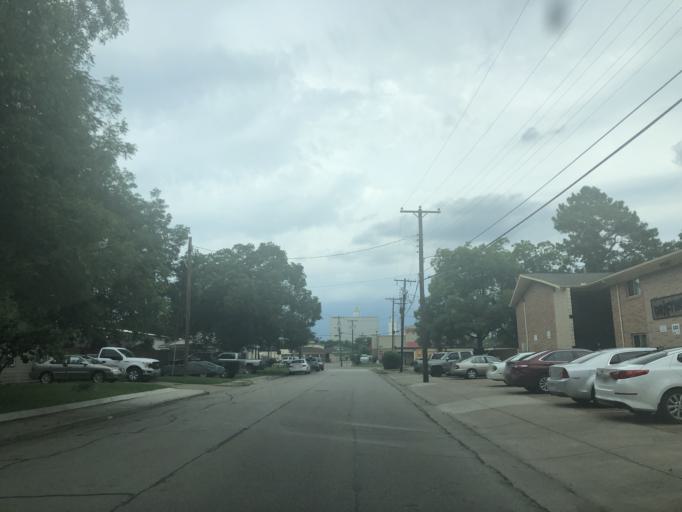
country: US
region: Texas
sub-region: Dallas County
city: Irving
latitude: 32.8117
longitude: -96.9382
